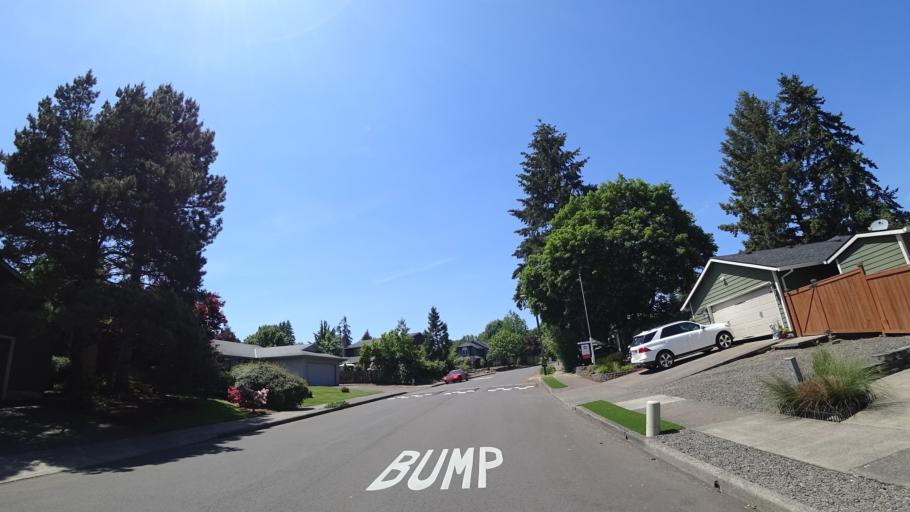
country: US
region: Oregon
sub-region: Washington County
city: Tigard
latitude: 45.4422
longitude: -122.7970
